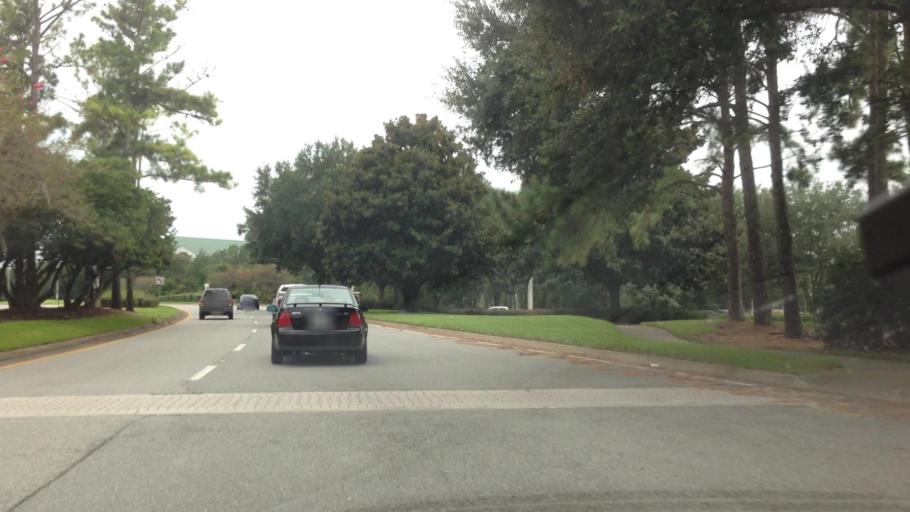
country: US
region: Florida
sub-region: Duval County
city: Jacksonville
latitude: 30.2617
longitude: -81.5496
